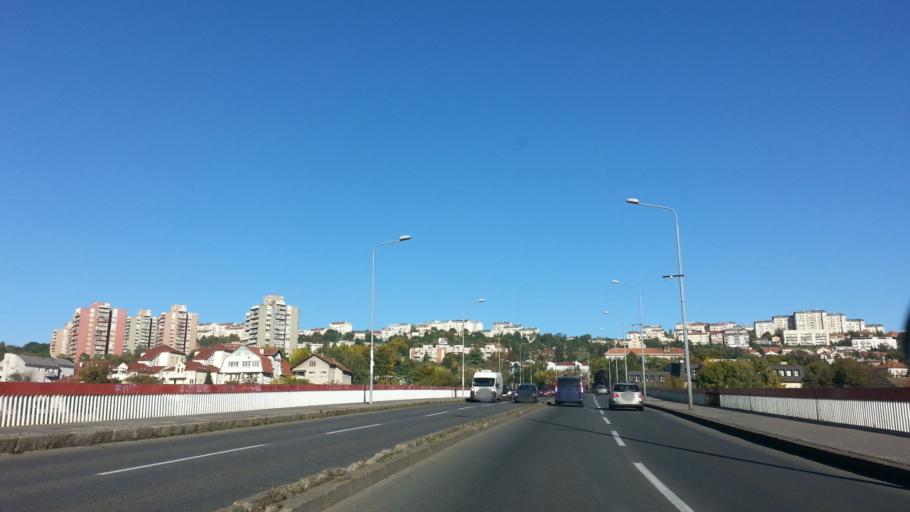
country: RS
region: Central Serbia
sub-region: Belgrade
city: Rakovica
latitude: 44.7438
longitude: 20.4428
